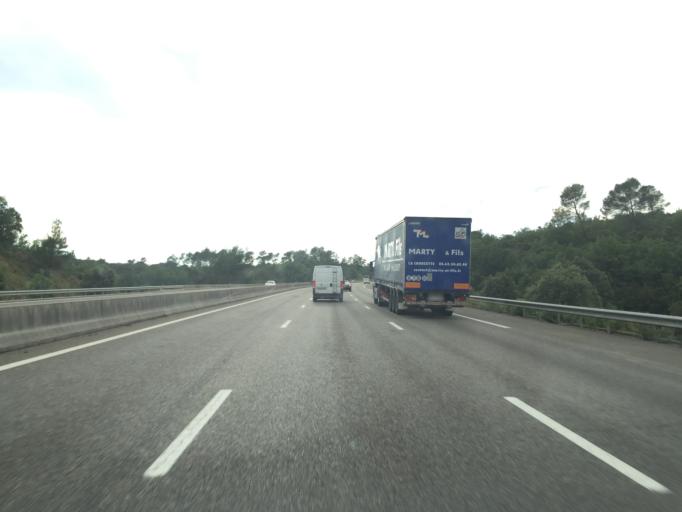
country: FR
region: Provence-Alpes-Cote d'Azur
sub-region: Departement du Var
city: Tourves
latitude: 43.4241
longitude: 5.9563
